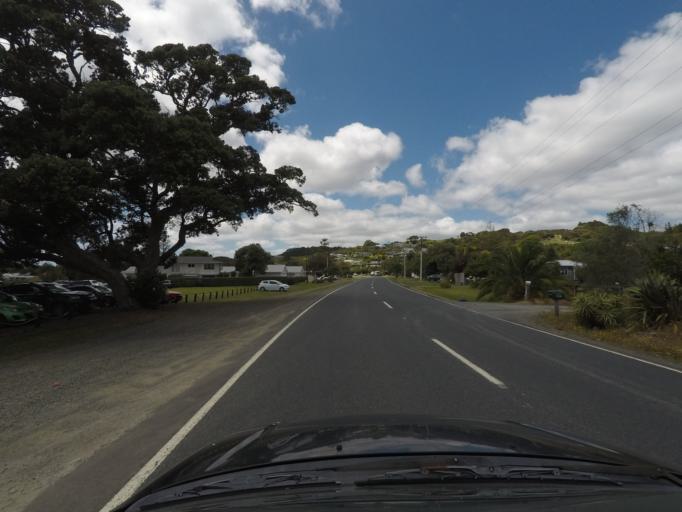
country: NZ
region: Northland
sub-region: Whangarei
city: Ruakaka
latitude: -36.0267
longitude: 174.5020
